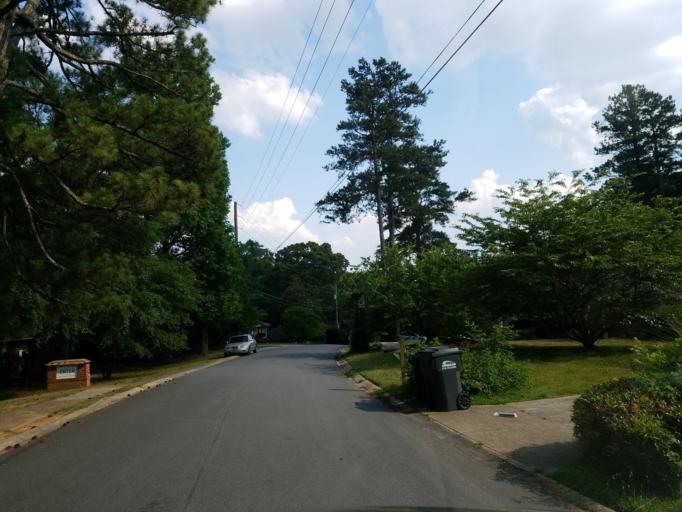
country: US
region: Georgia
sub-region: Cobb County
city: Marietta
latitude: 33.9497
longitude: -84.4949
